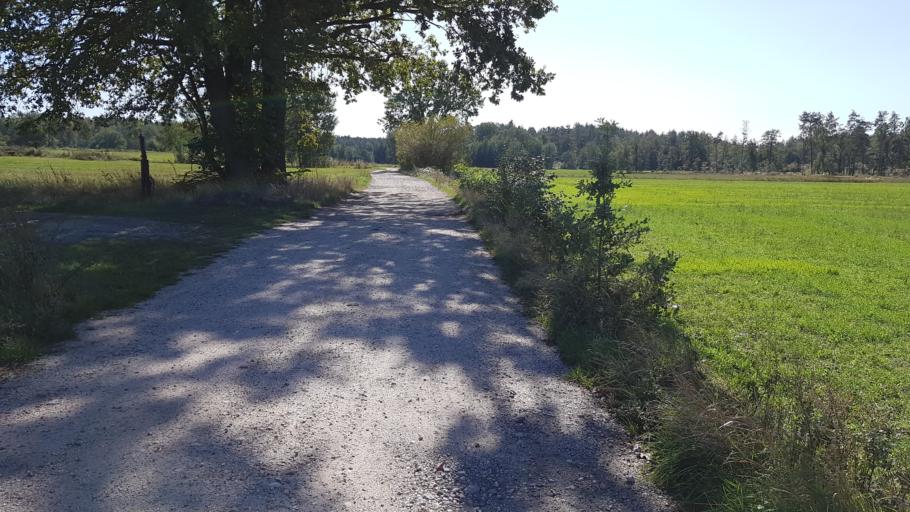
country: DE
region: Saxony
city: Hockendorf
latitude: 51.2419
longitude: 13.9184
